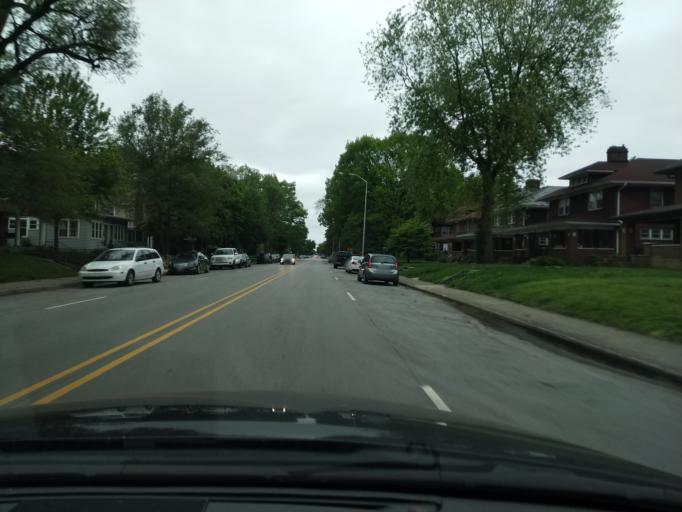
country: US
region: Indiana
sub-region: Marion County
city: Broad Ripple
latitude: 39.8304
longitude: -86.1499
